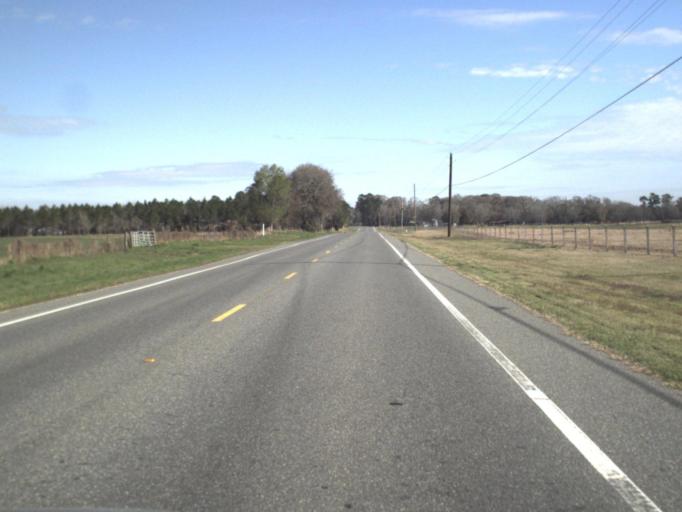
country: US
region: Florida
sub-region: Jackson County
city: Malone
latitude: 30.9377
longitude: -85.1652
